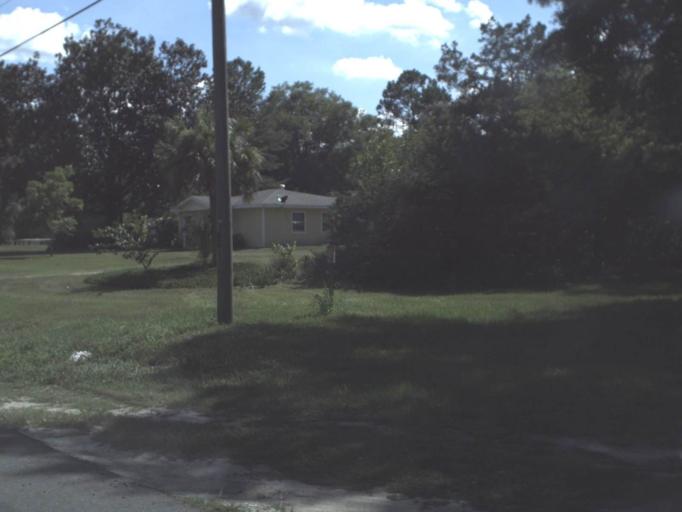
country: US
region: Florida
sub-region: Lafayette County
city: Mayo
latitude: 30.0603
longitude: -83.1752
